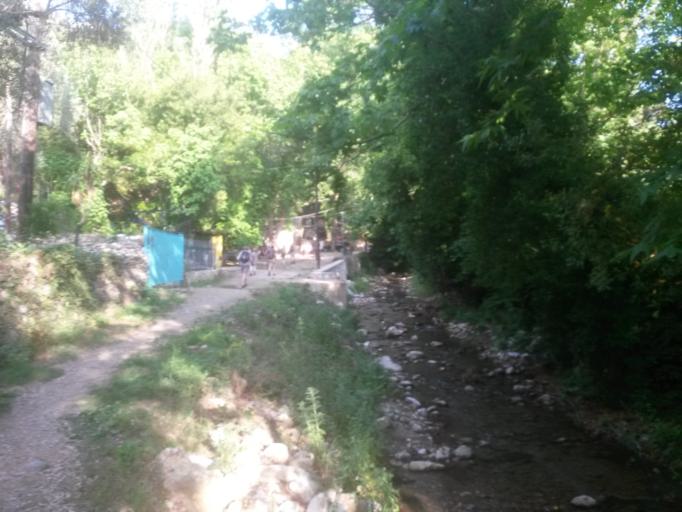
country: GR
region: North Aegean
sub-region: Nomos Lesvou
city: Agiasos
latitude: 39.0966
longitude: 26.4013
